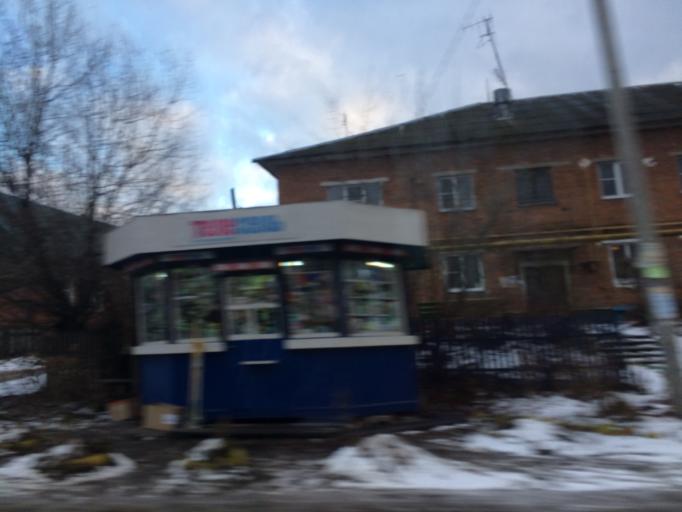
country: RU
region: Tula
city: Cherepet'
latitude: 54.1188
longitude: 36.3787
